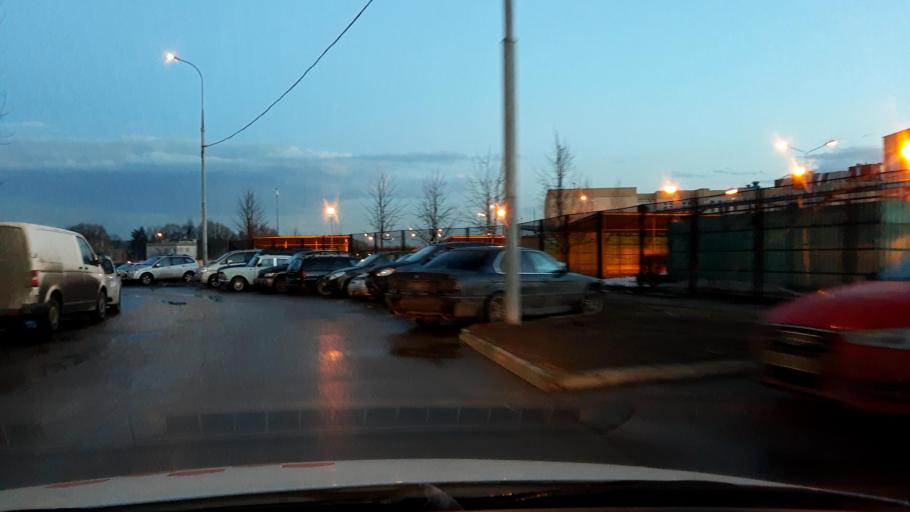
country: RU
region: Moskovskaya
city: Shcherbinka
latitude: 55.5374
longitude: 37.5372
